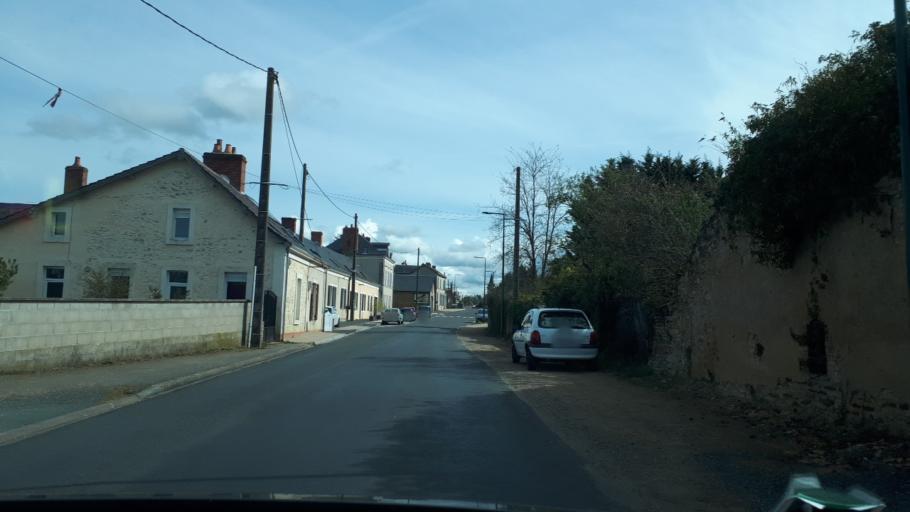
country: FR
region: Pays de la Loire
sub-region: Departement de la Sarthe
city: Ecommoy
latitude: 47.8252
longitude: 0.2650
